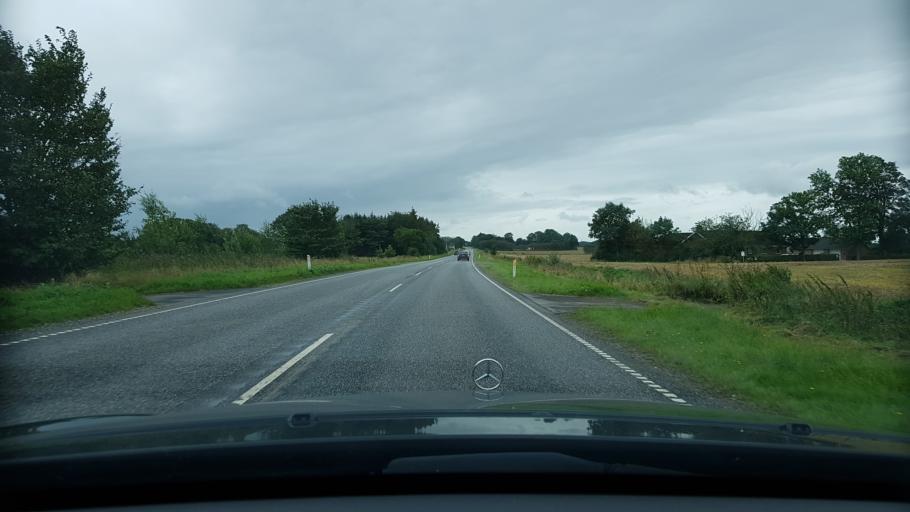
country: DK
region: Central Jutland
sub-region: Randers Kommune
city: Spentrup
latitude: 56.5461
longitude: 10.1012
